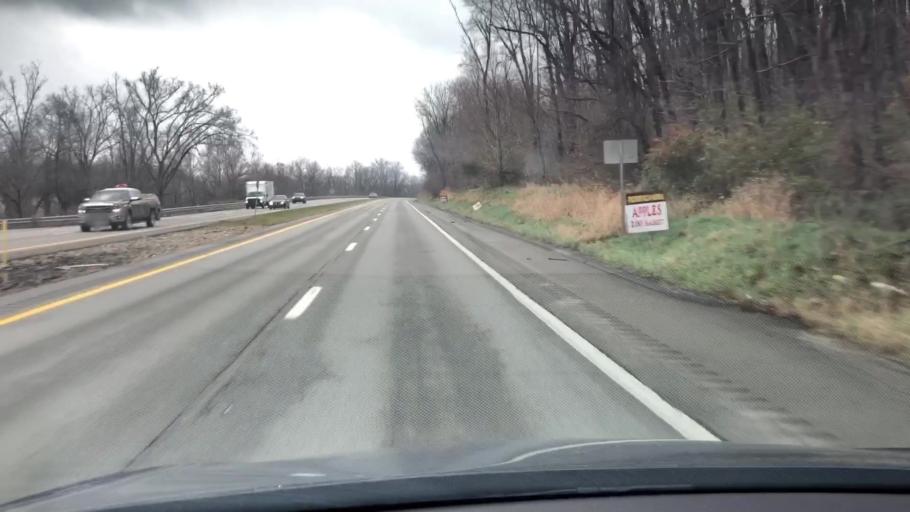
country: US
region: Pennsylvania
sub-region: Westmoreland County
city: Scottdale
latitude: 40.0787
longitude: -79.5623
